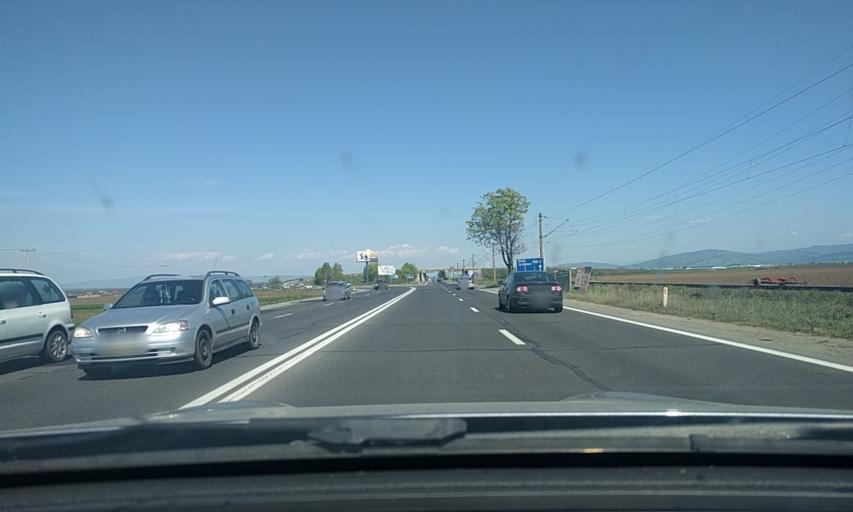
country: RO
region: Brasov
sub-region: Comuna Harman
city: Harman
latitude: 45.7081
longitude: 25.7021
